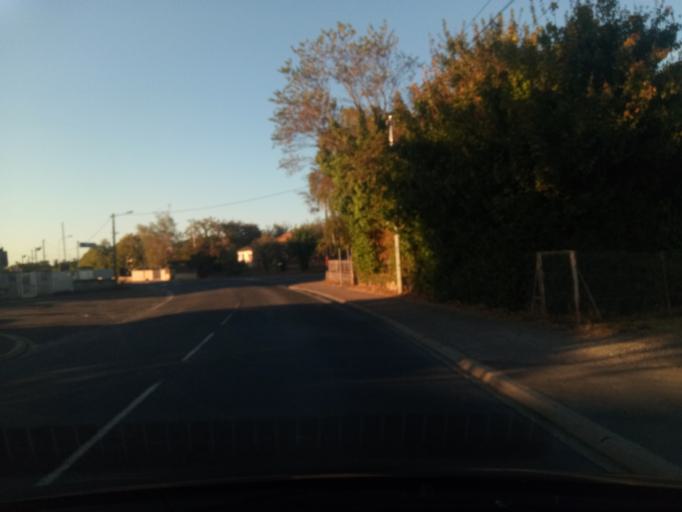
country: FR
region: Poitou-Charentes
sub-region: Departement de la Vienne
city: Montmorillon
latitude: 46.4219
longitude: 0.8610
